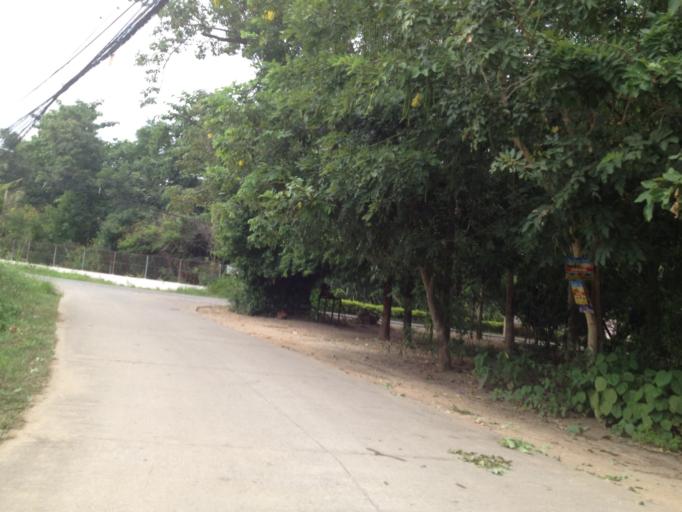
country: TH
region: Chiang Mai
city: Hang Dong
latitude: 18.6848
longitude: 98.9052
